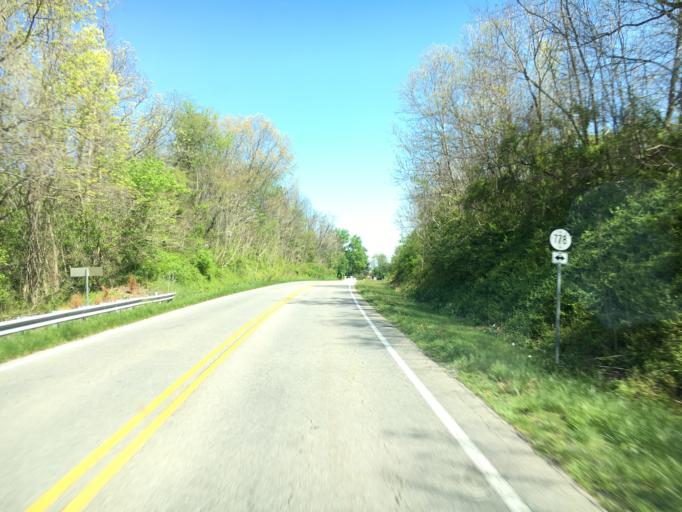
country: US
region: Virginia
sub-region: Rockingham County
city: Grottoes
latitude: 38.2148
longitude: -78.8323
